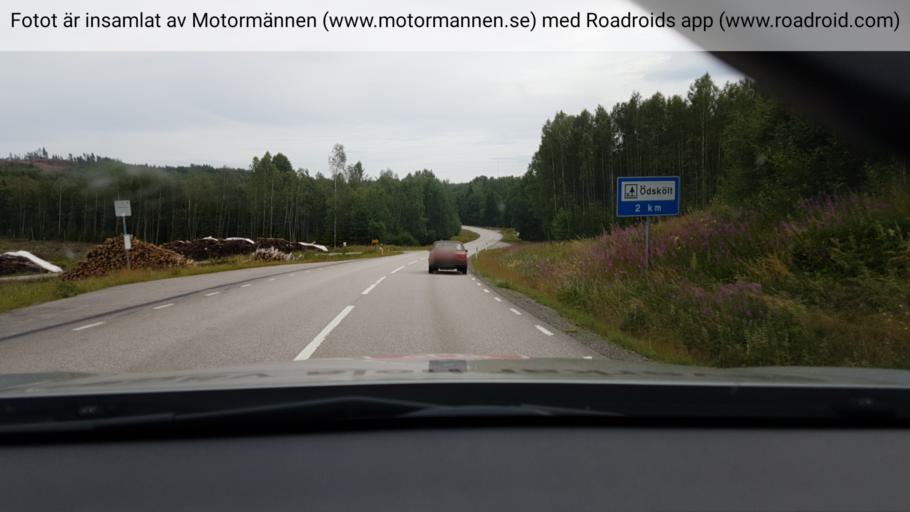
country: SE
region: Vaestra Goetaland
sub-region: Bengtsfors Kommun
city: Dals Langed
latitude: 58.8863
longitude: 12.2112
